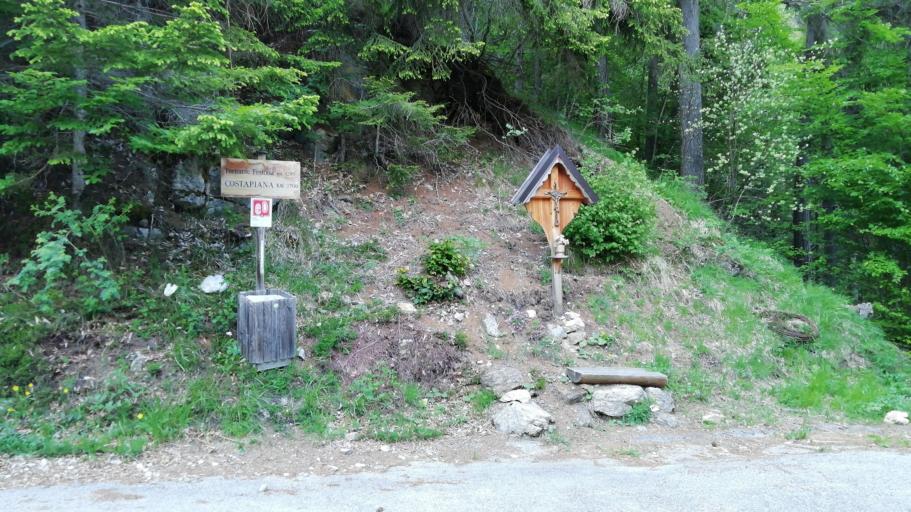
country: IT
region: Veneto
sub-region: Provincia di Belluno
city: Valle di Cadore
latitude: 46.4276
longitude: 12.3230
